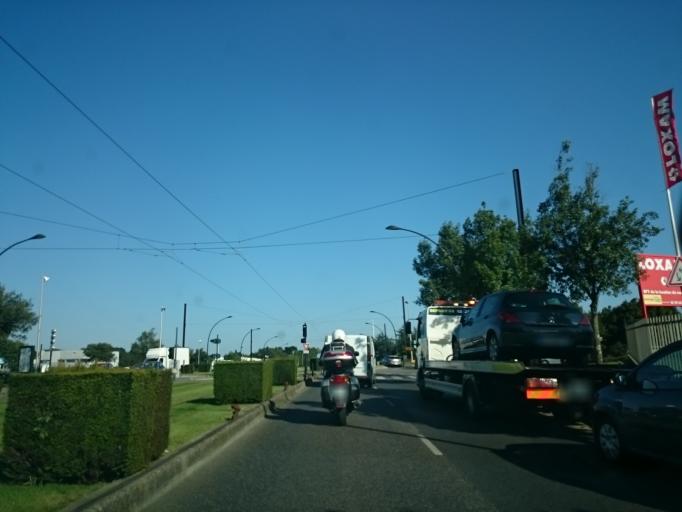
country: FR
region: Pays de la Loire
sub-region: Departement de la Loire-Atlantique
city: Saint-Herblain
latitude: 47.2198
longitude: -1.6247
